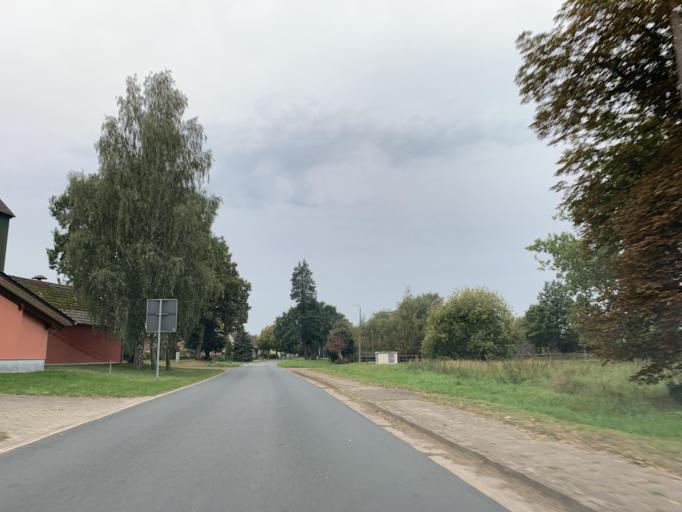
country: DE
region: Mecklenburg-Vorpommern
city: Woldegk
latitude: 53.3290
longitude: 13.5764
